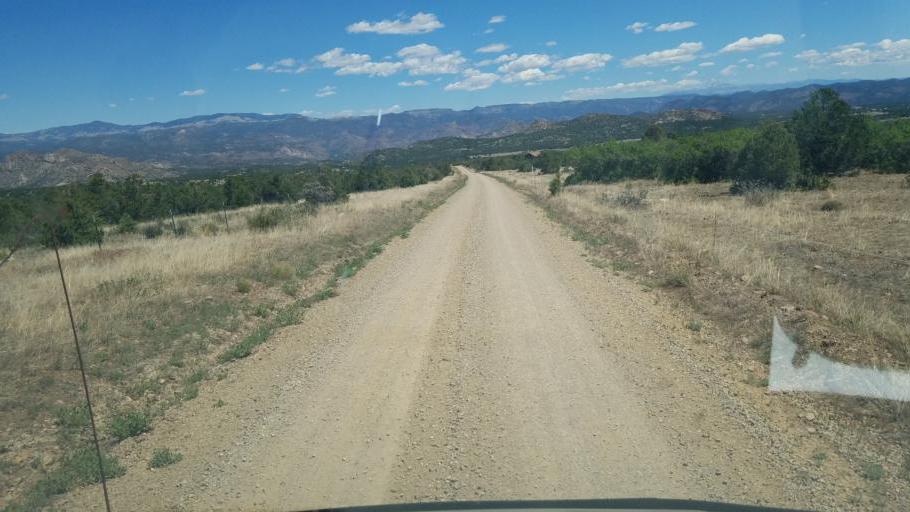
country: US
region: Colorado
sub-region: Custer County
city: Westcliffe
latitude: 38.2981
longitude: -105.6703
